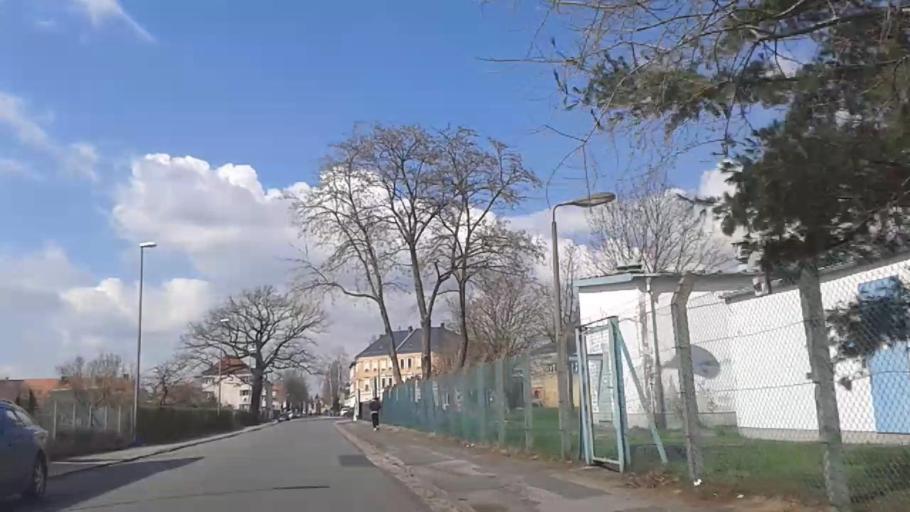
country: DE
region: Saxony
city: Radebeul
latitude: 51.0902
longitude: 13.6926
